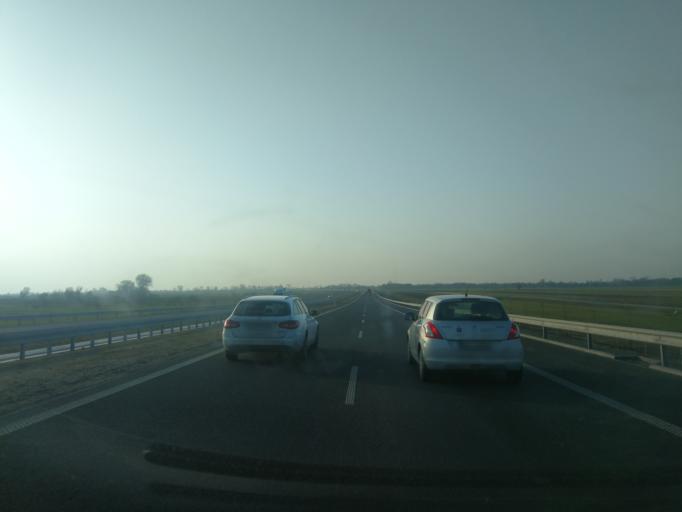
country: PL
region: Warmian-Masurian Voivodeship
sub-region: Powiat elblaski
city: Gronowo Elblaskie
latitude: 54.1677
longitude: 19.2330
